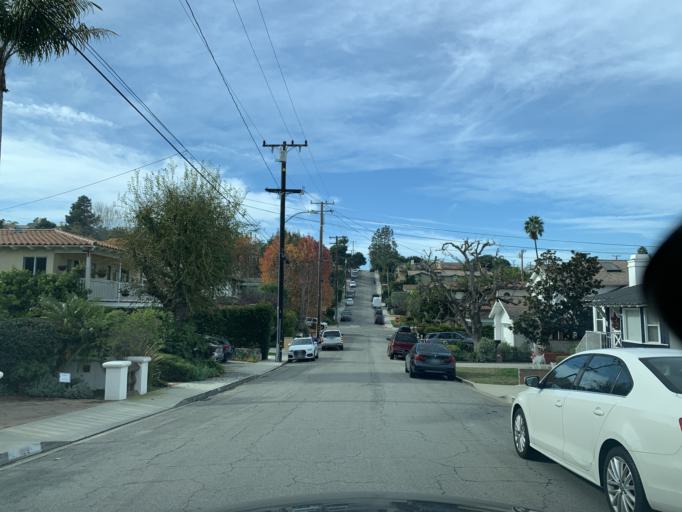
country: US
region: California
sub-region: Los Angeles County
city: Manhattan Beach
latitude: 33.8857
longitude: -118.3994
